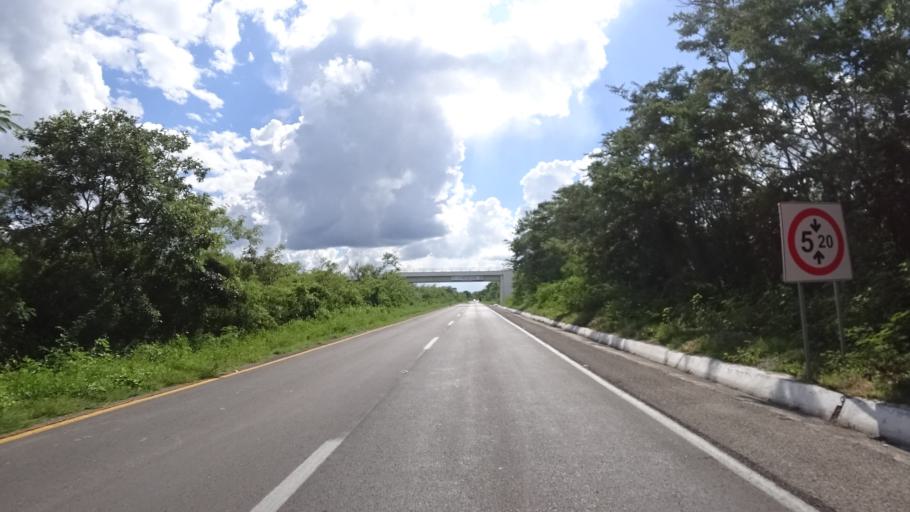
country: MX
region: Yucatan
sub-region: Kantunil
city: Kantunil
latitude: 20.8046
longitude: -89.0421
